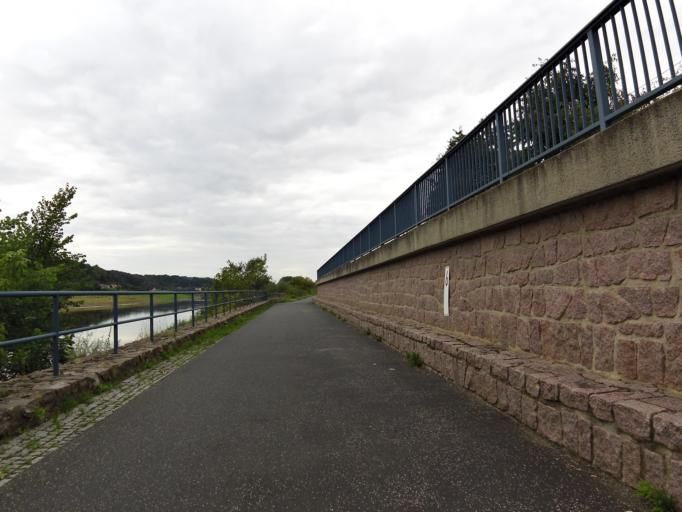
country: DE
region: Saxony
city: Meissen
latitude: 51.1865
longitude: 13.4466
